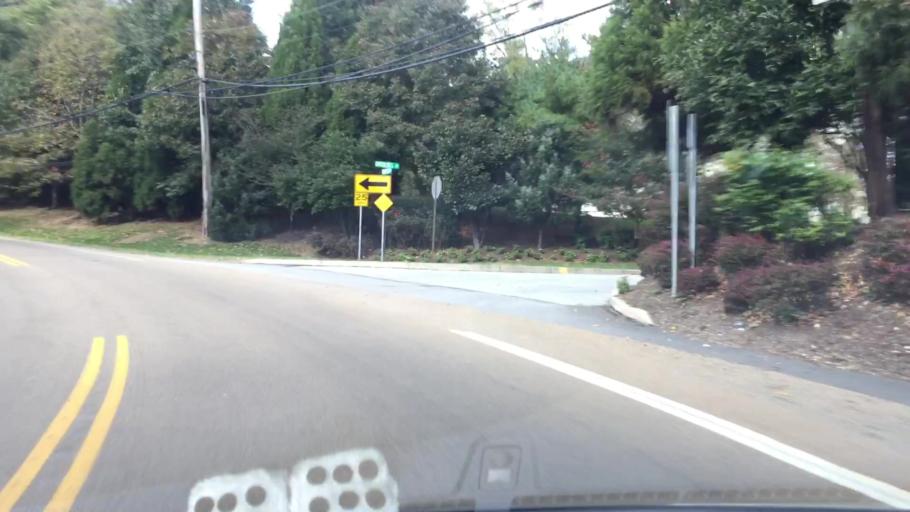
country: US
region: Pennsylvania
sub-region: Delaware County
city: Lima
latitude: 39.9521
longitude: -75.4158
